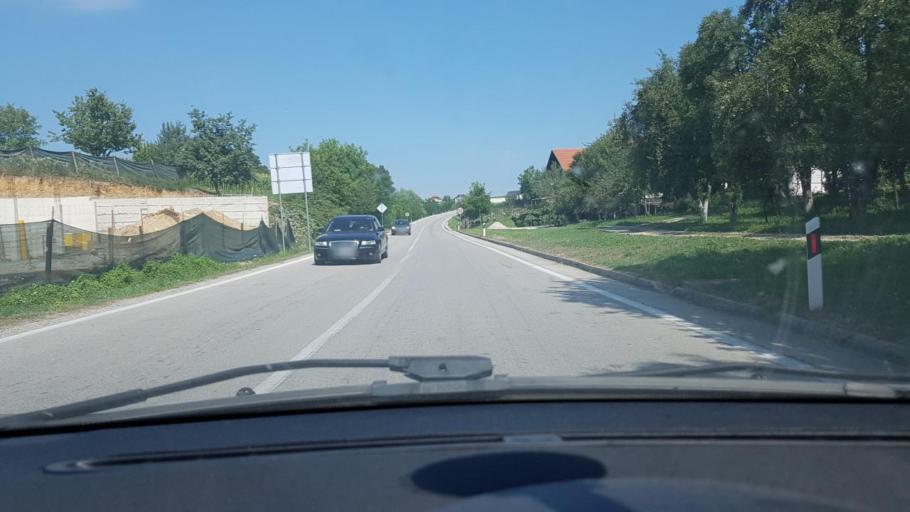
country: BA
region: Federation of Bosnia and Herzegovina
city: Velika Kladusa
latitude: 45.1932
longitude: 15.8120
